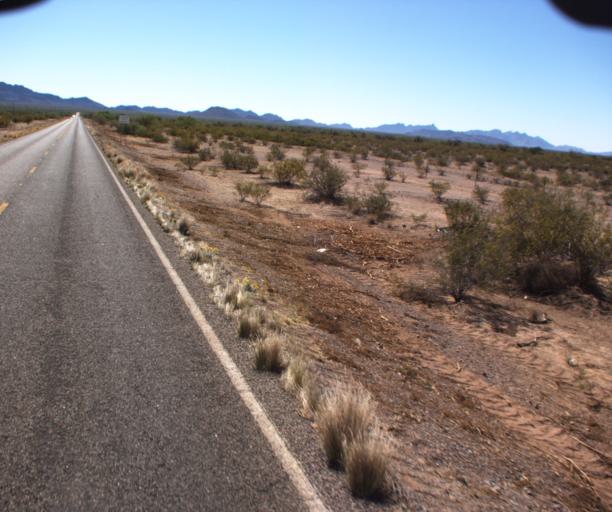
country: US
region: Arizona
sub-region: Pima County
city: Ajo
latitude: 32.3384
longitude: -112.7972
